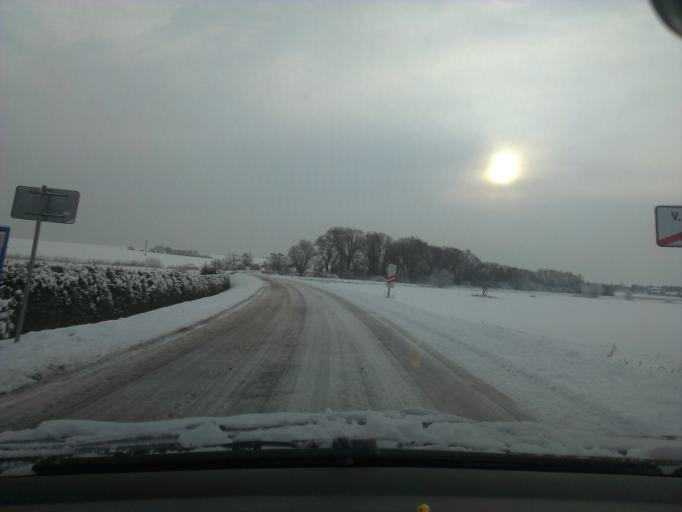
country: SK
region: Trnavsky
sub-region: Okres Trnava
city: Piestany
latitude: 48.5175
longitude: 17.9747
